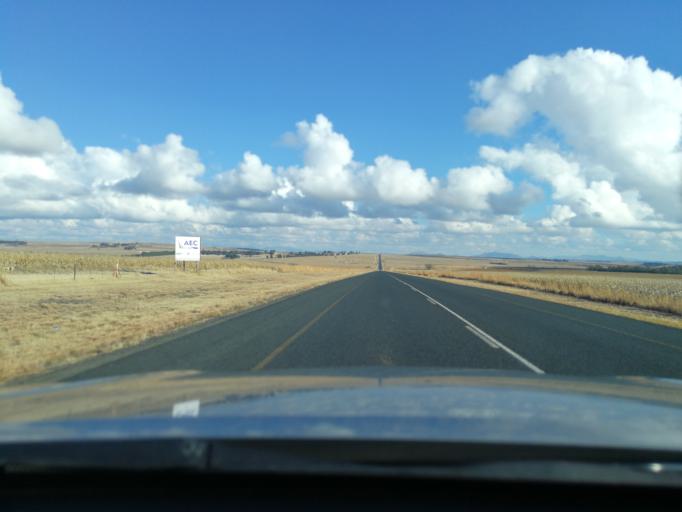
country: ZA
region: Orange Free State
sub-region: Thabo Mofutsanyana District Municipality
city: Bethlehem
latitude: -28.0882
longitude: 28.3551
